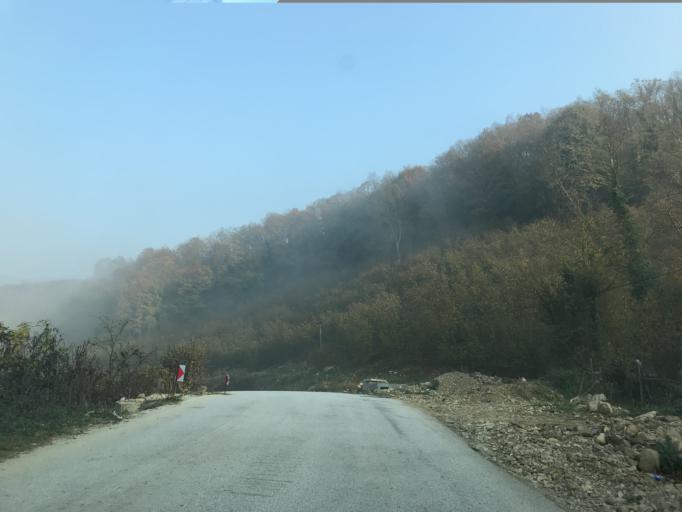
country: TR
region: Duzce
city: Cumayeri
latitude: 40.9012
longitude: 30.9549
